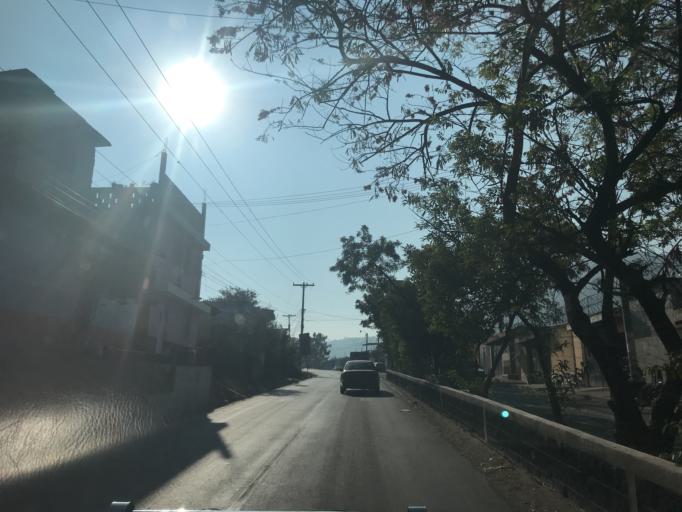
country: GT
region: Guatemala
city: Amatitlan
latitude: 14.4799
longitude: -90.6140
